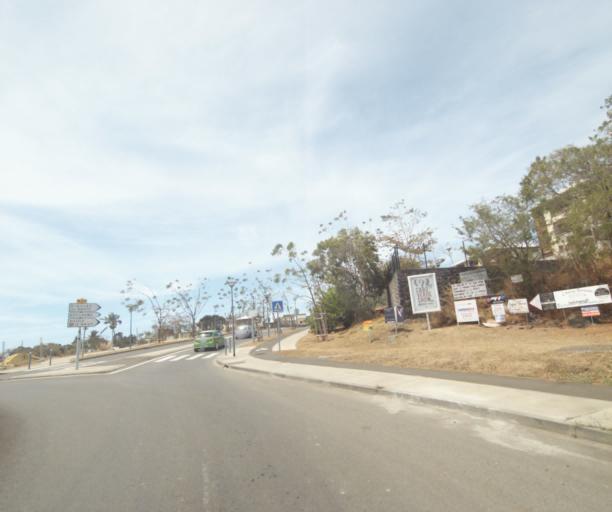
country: RE
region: Reunion
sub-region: Reunion
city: Saint-Paul
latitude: -21.0429
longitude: 55.2521
